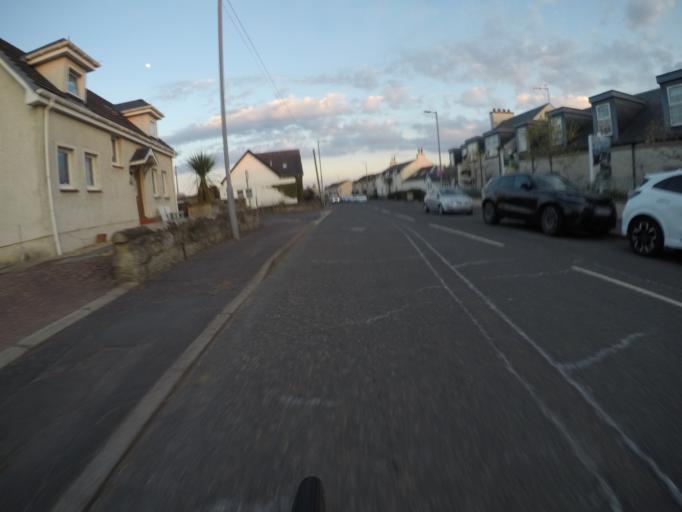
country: GB
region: Scotland
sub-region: South Ayrshire
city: Troon
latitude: 55.5519
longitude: -4.6254
